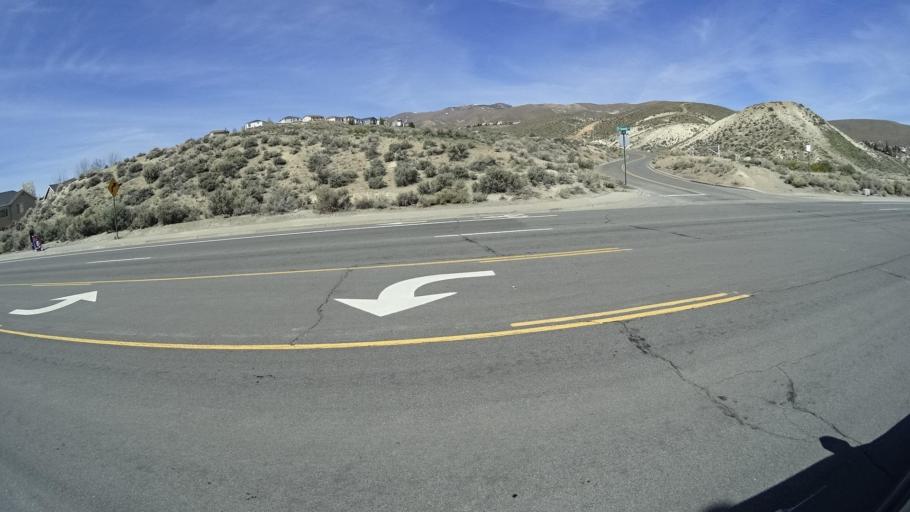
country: US
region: Nevada
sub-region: Washoe County
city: Mogul
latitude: 39.5360
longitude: -119.8750
